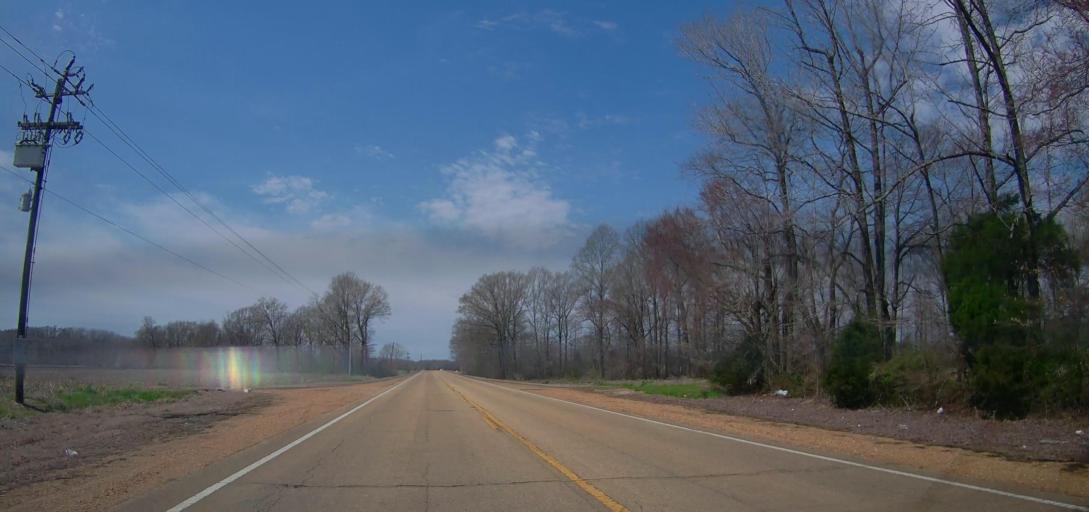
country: US
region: Mississippi
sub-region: Benton County
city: Ashland
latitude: 34.6190
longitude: -89.2189
